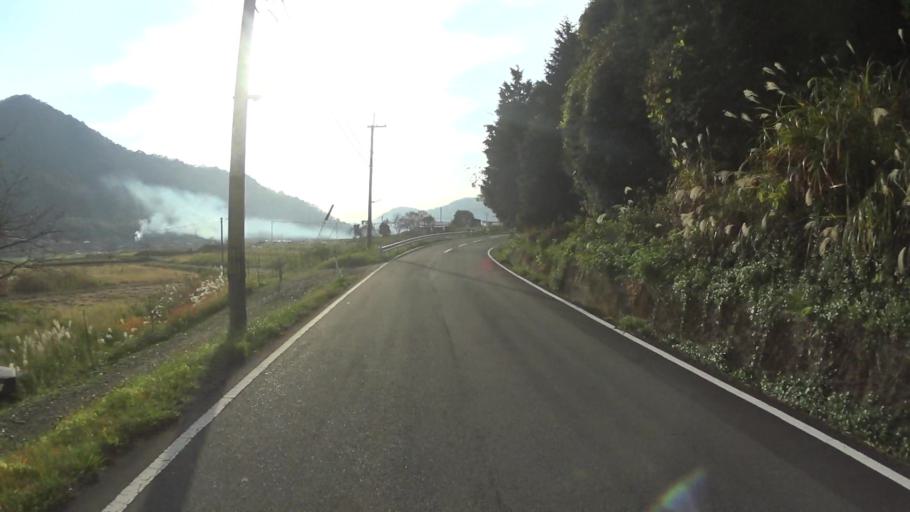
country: JP
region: Kyoto
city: Maizuru
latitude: 35.5276
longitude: 135.4214
